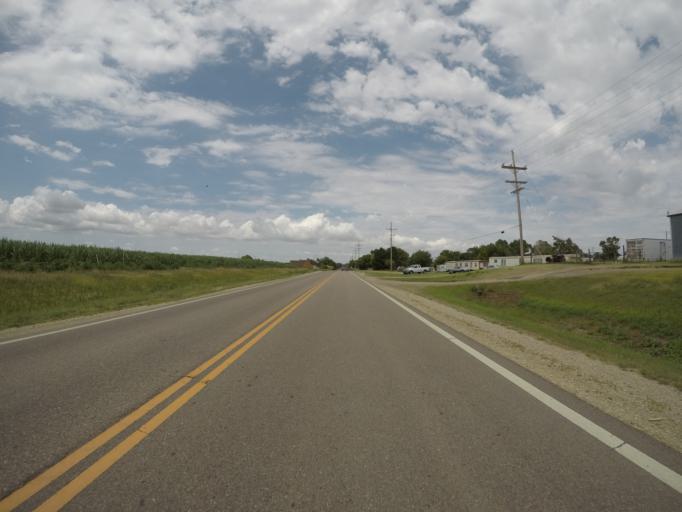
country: US
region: Kansas
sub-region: Rawlins County
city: Atwood
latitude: 39.7970
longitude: -101.0469
